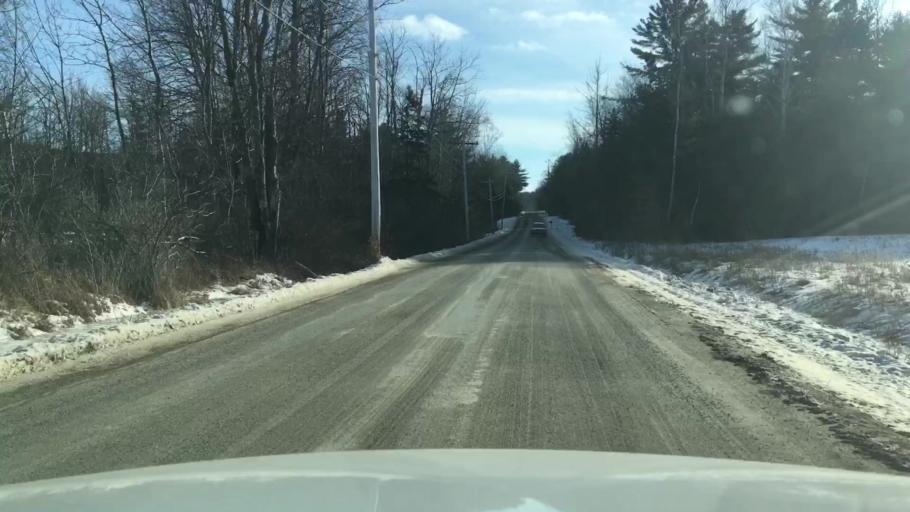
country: US
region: Maine
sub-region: Penobscot County
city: Holden
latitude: 44.7744
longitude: -68.5849
